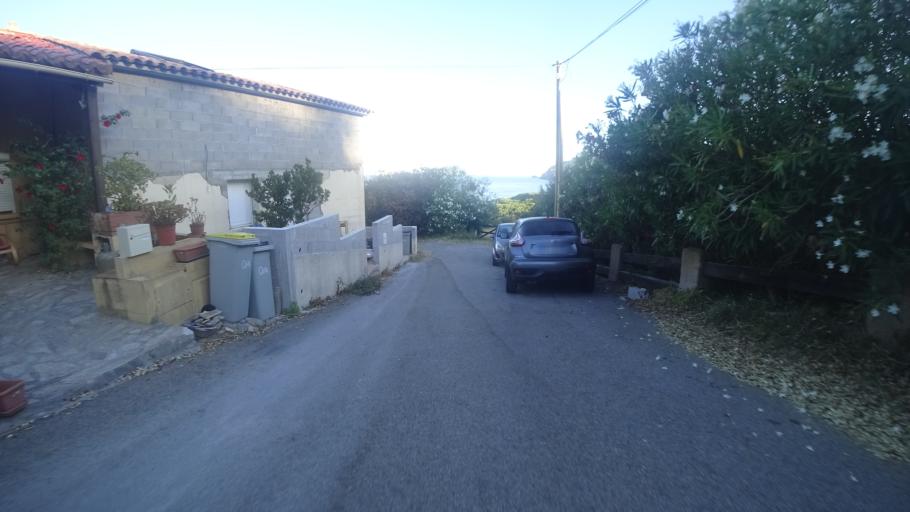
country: FR
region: Corsica
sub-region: Departement de la Corse-du-Sud
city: Alata
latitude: 41.9789
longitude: 8.6665
